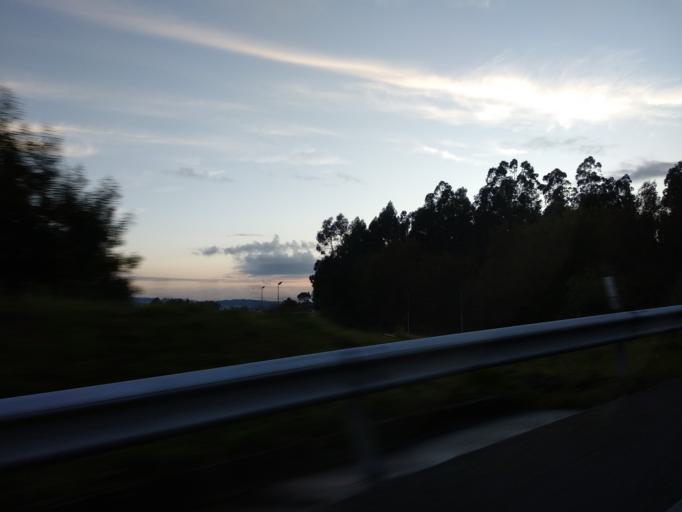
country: PT
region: Braga
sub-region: Braga
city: Oliveira
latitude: 41.4826
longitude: -8.4626
